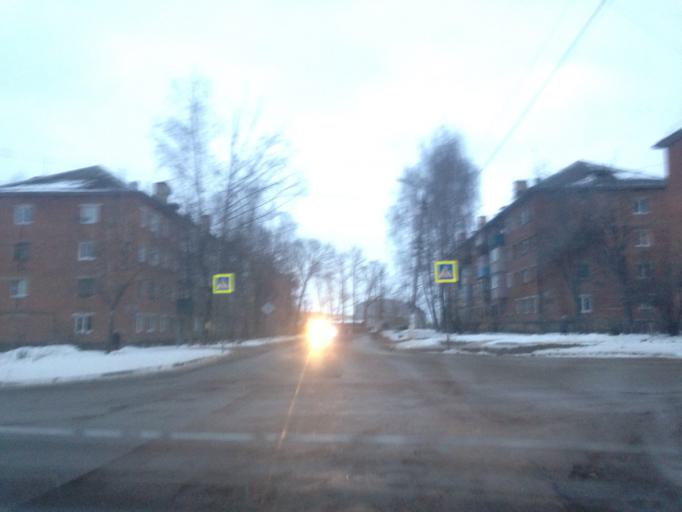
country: RU
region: Tula
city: Shchekino
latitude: 53.9985
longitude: 37.5270
